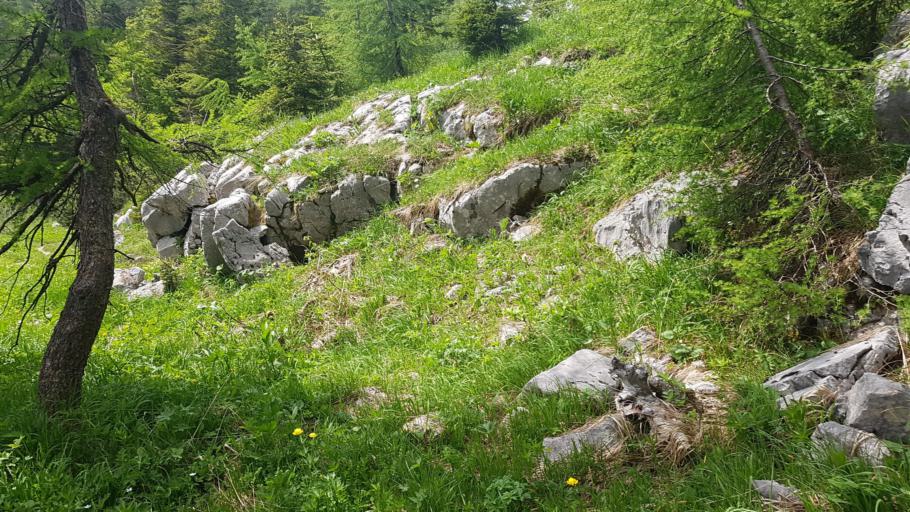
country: IT
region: Friuli Venezia Giulia
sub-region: Provincia di Udine
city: Pontebba
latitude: 46.5447
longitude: 13.2716
